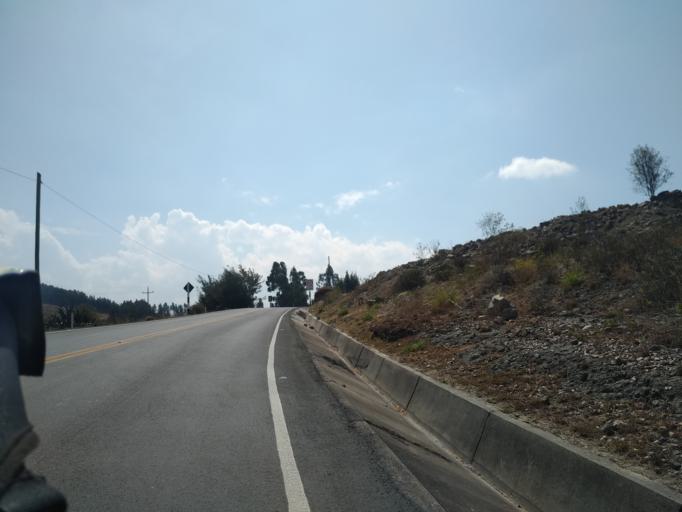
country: PE
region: Cajamarca
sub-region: Provincia de Cajamarca
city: Namora
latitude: -7.2052
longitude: -78.3828
